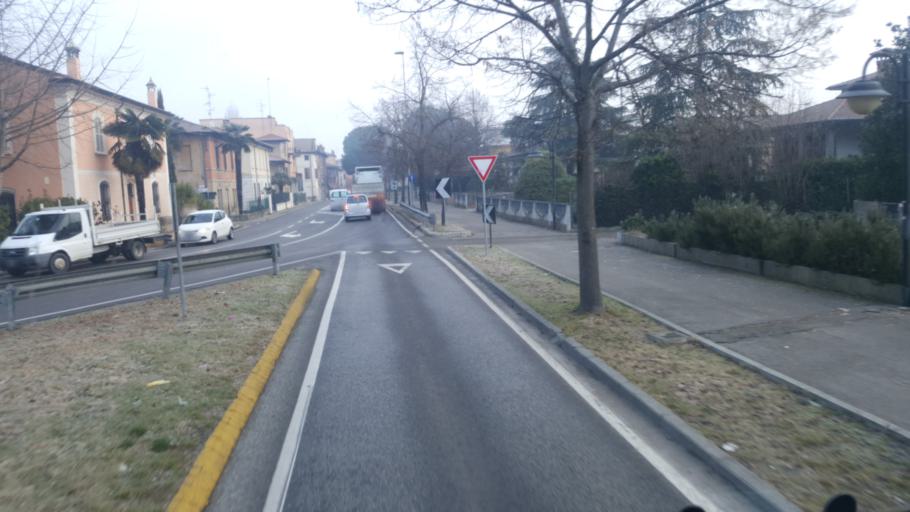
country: IT
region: Emilia-Romagna
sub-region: Provincia di Ravenna
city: Bagnacavallo
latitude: 44.4125
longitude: 11.9722
